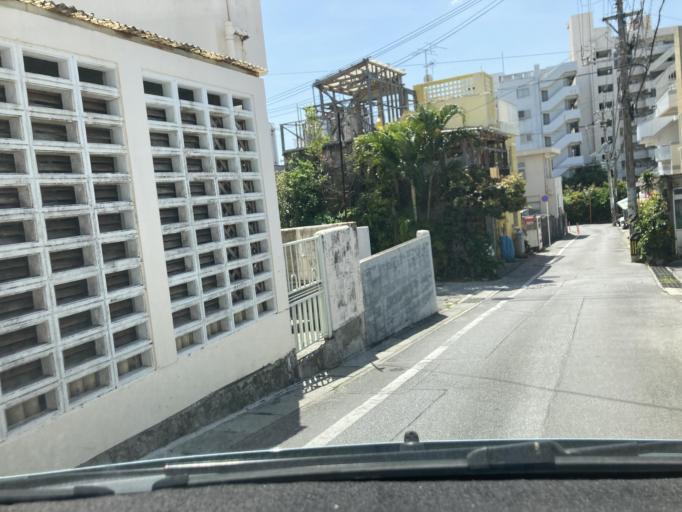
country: JP
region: Okinawa
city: Tomigusuku
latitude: 26.1986
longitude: 127.6905
